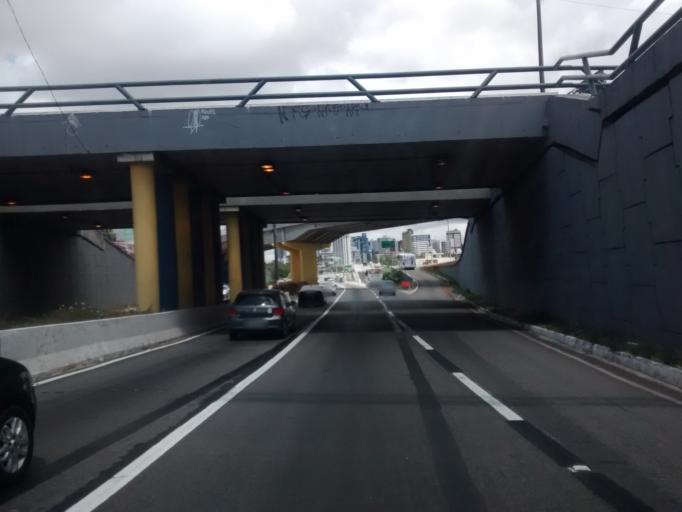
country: BR
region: Rio Grande do Norte
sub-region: Natal
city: Natal
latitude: -5.8257
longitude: -35.2099
